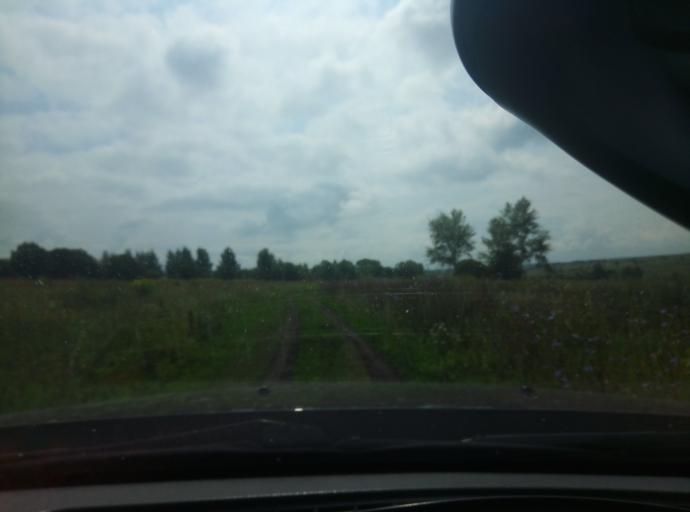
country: RU
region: Tula
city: Shvartsevskiy
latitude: 54.0807
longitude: 38.0213
